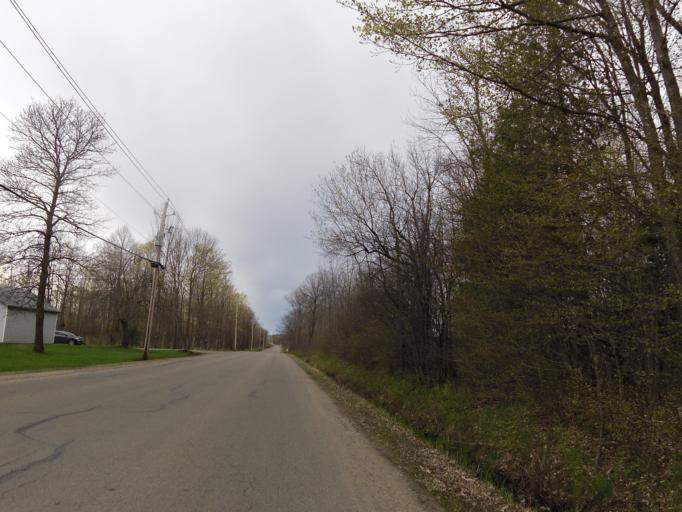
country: CA
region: Ontario
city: Hawkesbury
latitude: 45.6248
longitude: -74.5770
